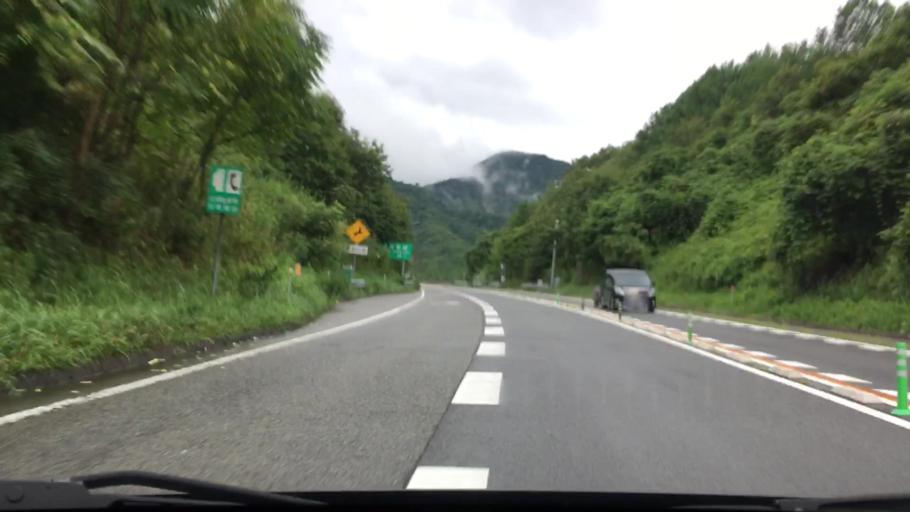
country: JP
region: Hyogo
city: Toyooka
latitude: 35.3116
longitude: 134.8289
